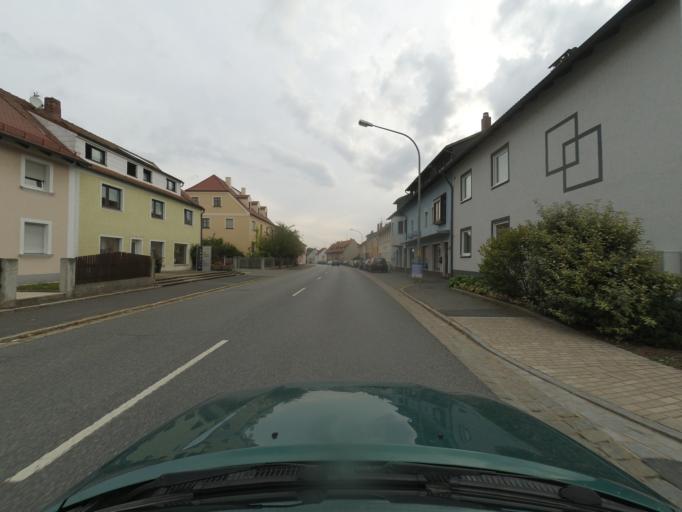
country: DE
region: Bavaria
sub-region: Upper Palatinate
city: Schnaittenbach
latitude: 49.5480
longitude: 12.0039
